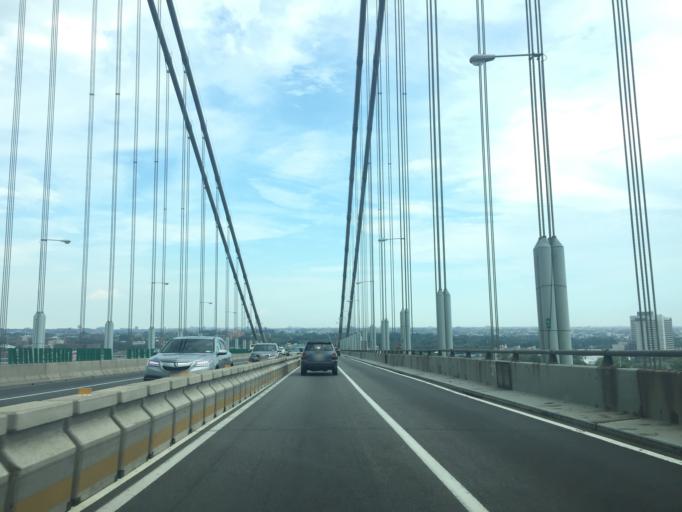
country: US
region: New York
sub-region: Kings County
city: Bensonhurst
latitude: 40.6088
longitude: -74.0372
